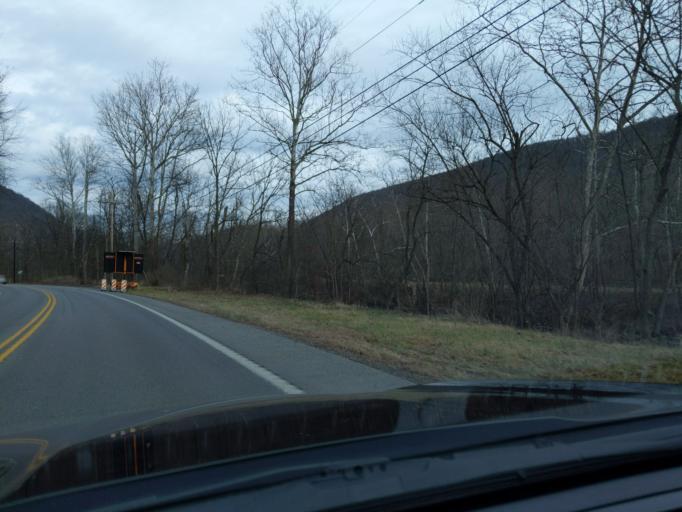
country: US
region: Pennsylvania
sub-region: Blair County
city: Williamsburg
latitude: 40.4754
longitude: -78.2655
